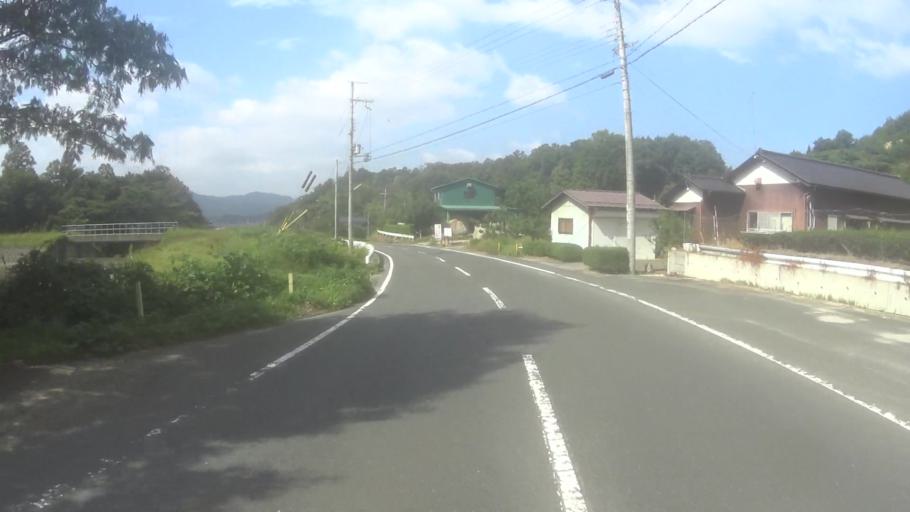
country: JP
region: Kyoto
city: Miyazu
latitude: 35.5875
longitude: 135.1130
